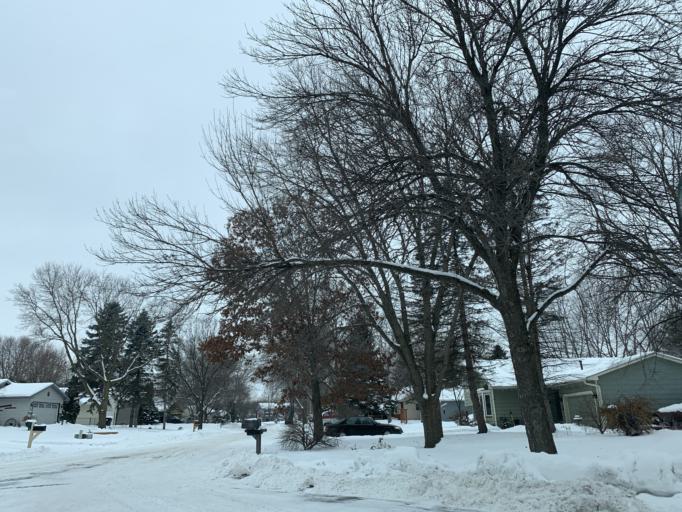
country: US
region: Minnesota
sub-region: Anoka County
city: Coon Rapids
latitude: 45.1640
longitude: -93.2977
